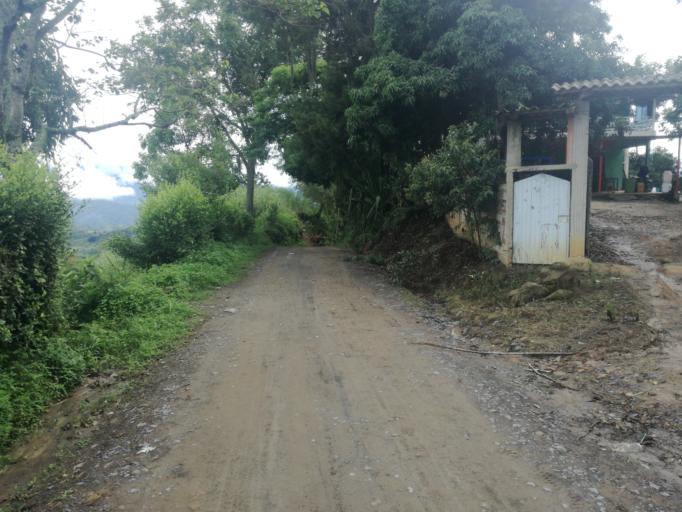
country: CO
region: Boyaca
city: Santana
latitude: 6.0637
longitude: -73.4835
